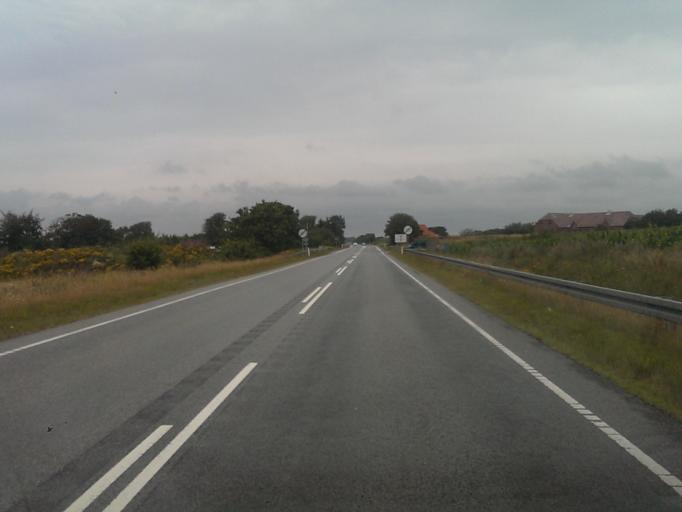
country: DK
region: South Denmark
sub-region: Esbjerg Kommune
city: Tjaereborg
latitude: 55.5494
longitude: 8.6319
